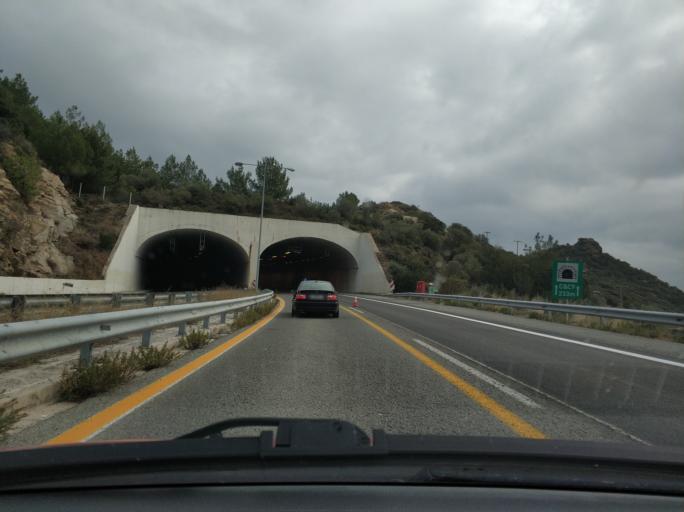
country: GR
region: East Macedonia and Thrace
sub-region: Nomos Kavalas
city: Palaio Tsifliki
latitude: 40.9098
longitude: 24.3550
